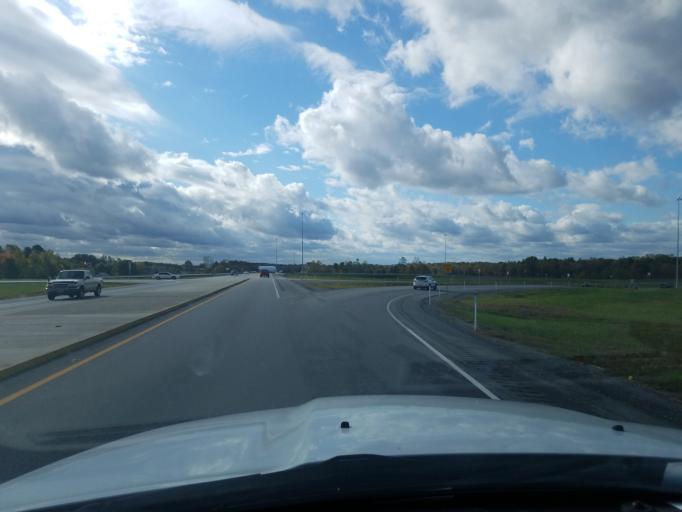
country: US
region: Kentucky
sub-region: Russell County
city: Russell Springs
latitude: 37.0540
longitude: -85.0703
